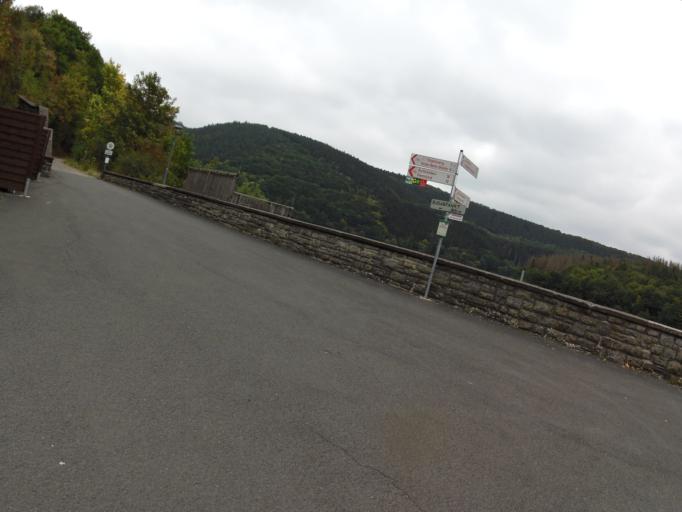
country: DE
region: North Rhine-Westphalia
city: Heimbach
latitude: 50.6043
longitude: 6.4206
